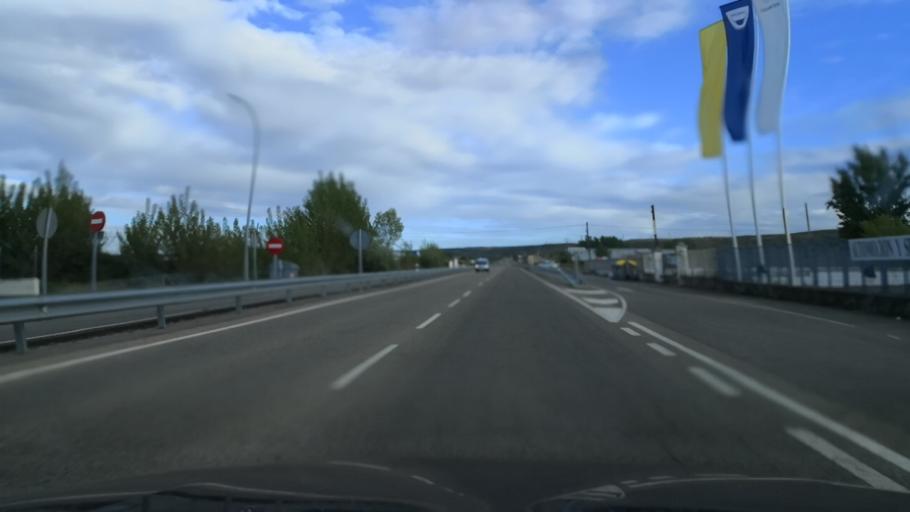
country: ES
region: Extremadura
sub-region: Provincia de Caceres
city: Coria
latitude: 39.9690
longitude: -6.5212
